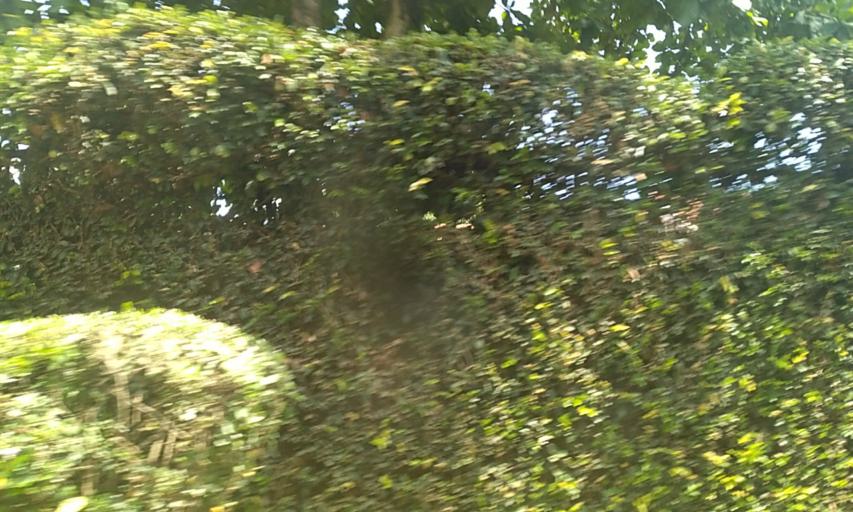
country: UG
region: Central Region
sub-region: Kampala District
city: Kampala
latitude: 0.3252
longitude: 32.5979
